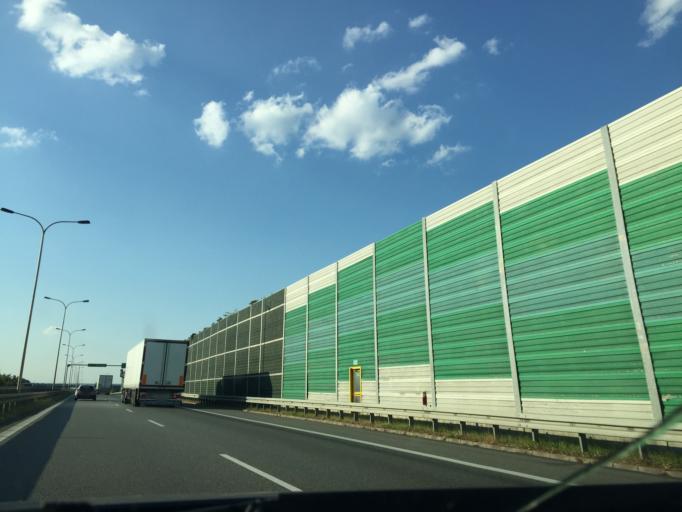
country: PL
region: Masovian Voivodeship
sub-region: Powiat bialobrzeski
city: Sucha
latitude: 51.6060
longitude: 20.9847
